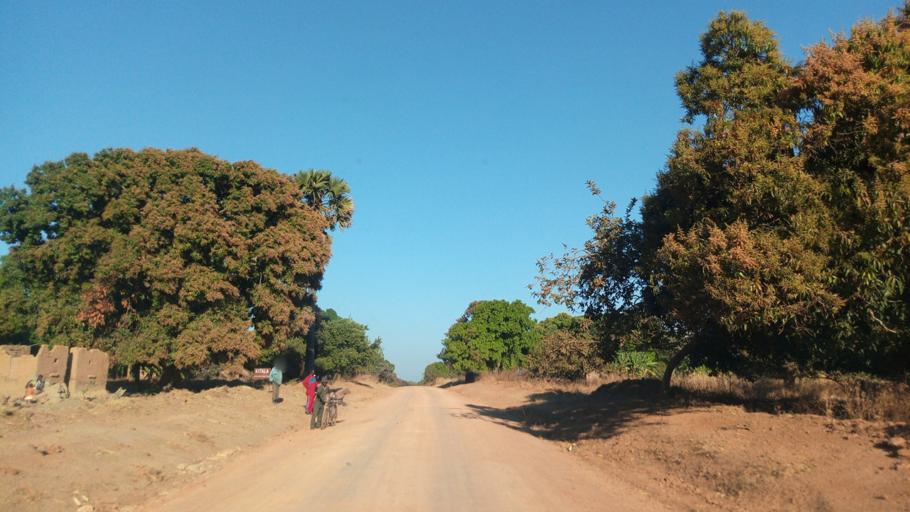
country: ZM
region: Luapula
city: Mwense
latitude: -10.4467
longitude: 28.5650
